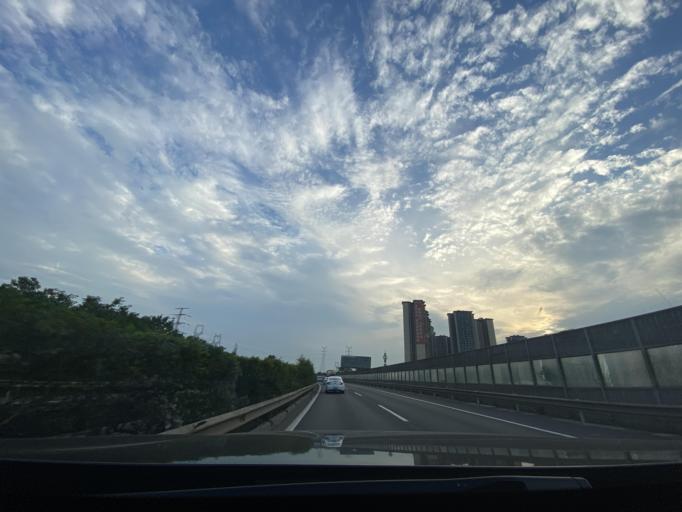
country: CN
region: Sichuan
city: Deyang
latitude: 31.0814
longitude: 104.3872
